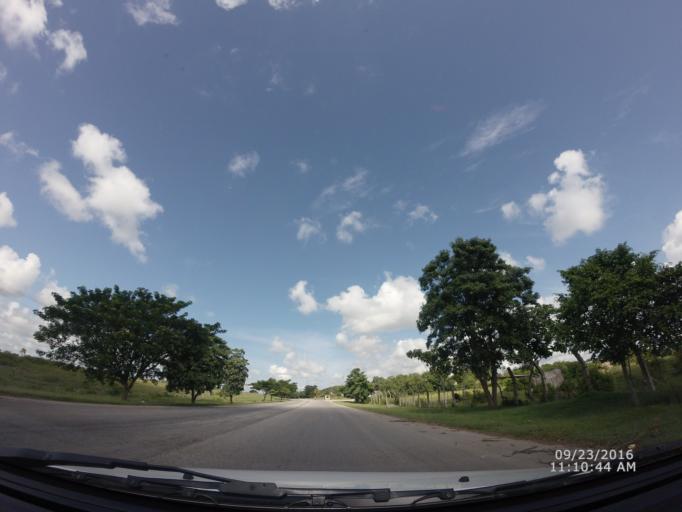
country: CU
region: La Habana
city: Arroyo Naranjo
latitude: 23.0222
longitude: -82.2598
